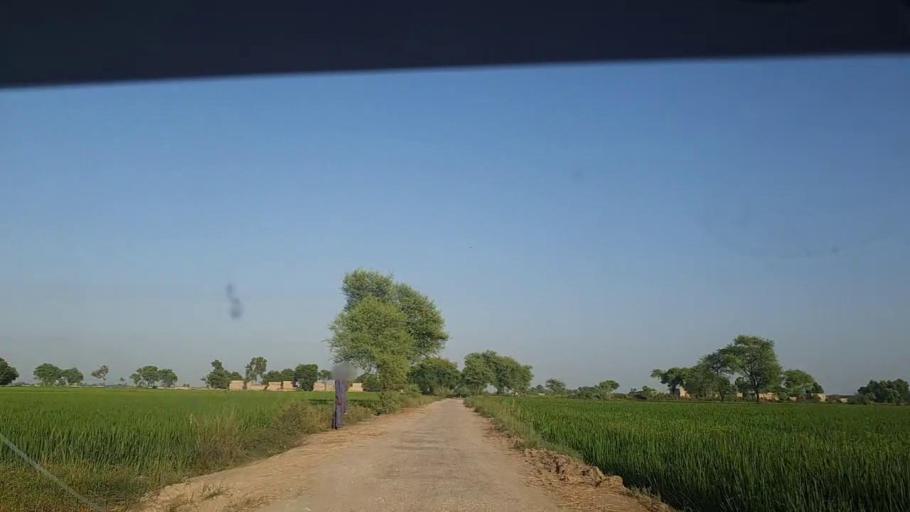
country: PK
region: Sindh
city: Thul
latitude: 28.2143
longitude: 68.8748
